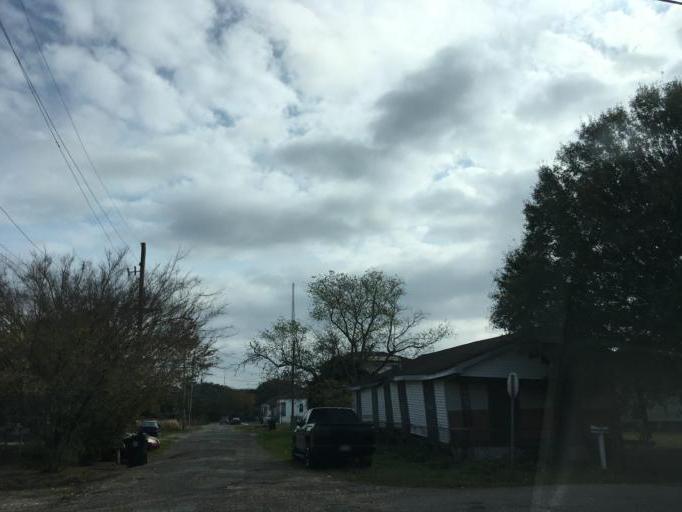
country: US
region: Louisiana
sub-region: Orleans Parish
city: New Orleans
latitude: 29.9868
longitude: -90.0558
